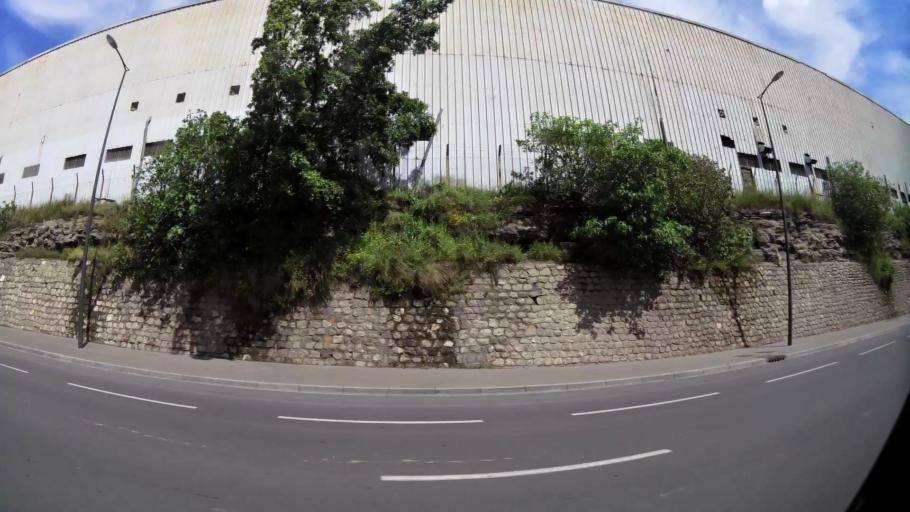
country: MA
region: Grand Casablanca
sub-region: Casablanca
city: Casablanca
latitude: 33.6016
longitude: -7.5573
